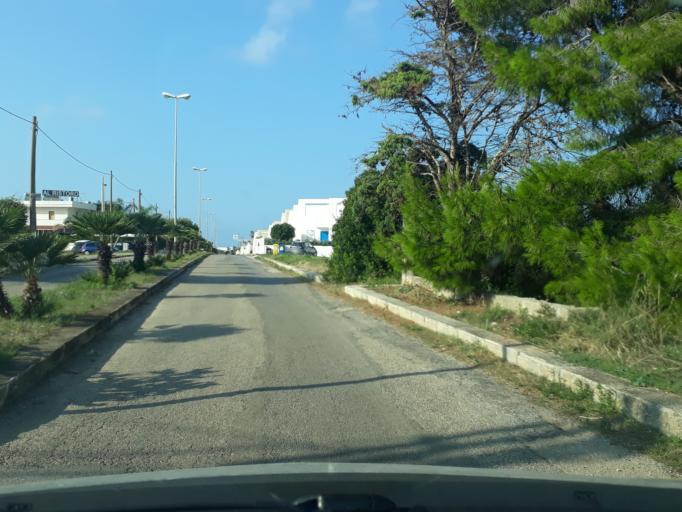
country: IT
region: Apulia
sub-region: Provincia di Brindisi
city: Carovigno
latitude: 40.7554
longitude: 17.6944
